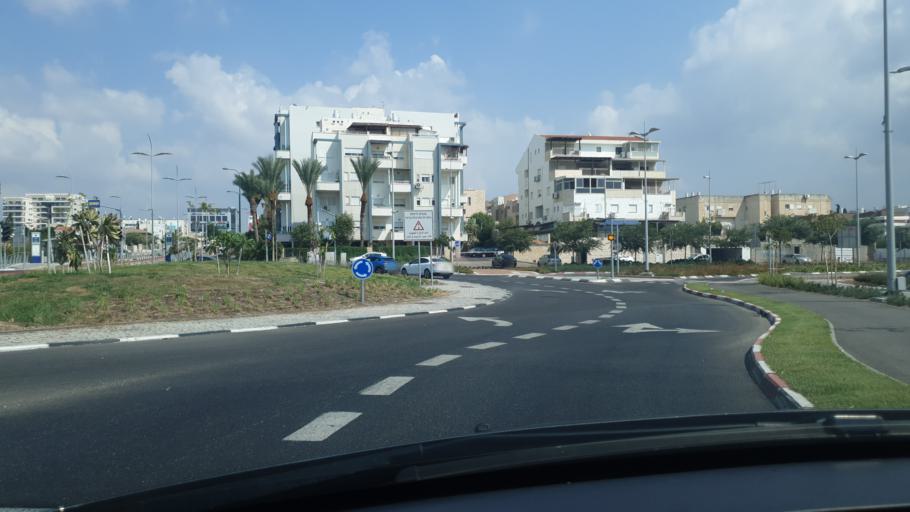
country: IL
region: Haifa
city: Qiryat Ata
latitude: 32.8126
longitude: 35.0995
